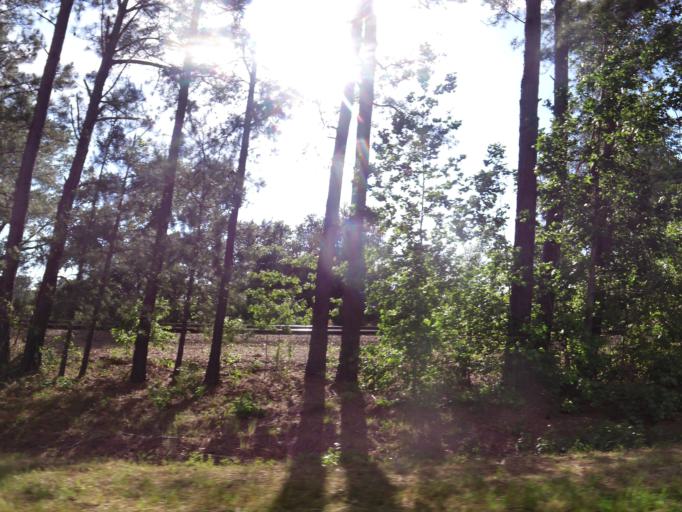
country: US
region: South Carolina
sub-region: Hampton County
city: Estill
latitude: 32.8454
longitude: -81.2391
